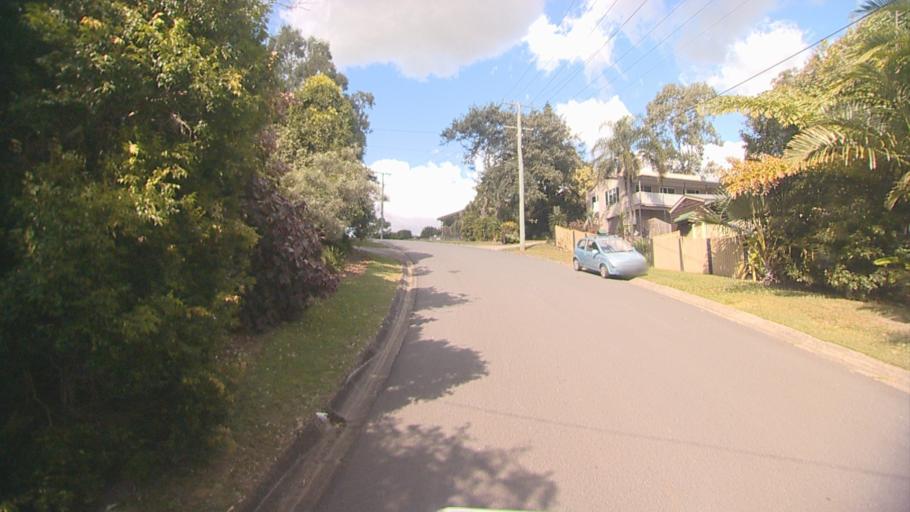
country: AU
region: Queensland
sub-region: Logan
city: Beenleigh
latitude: -27.6776
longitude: 153.2033
